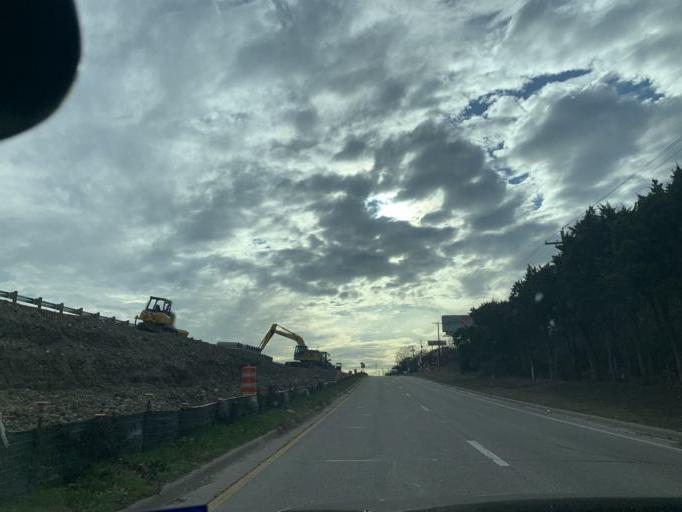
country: US
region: Texas
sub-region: Dallas County
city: Duncanville
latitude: 32.6243
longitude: -96.9099
